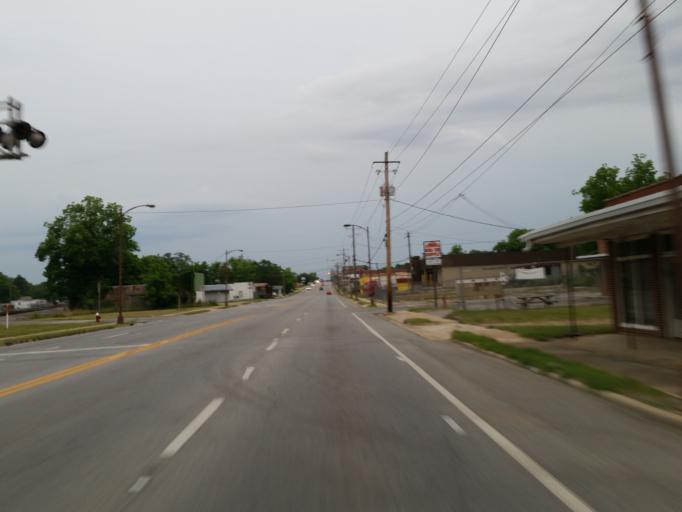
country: US
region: Georgia
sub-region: Crisp County
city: Cordele
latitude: 31.9609
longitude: -83.7826
